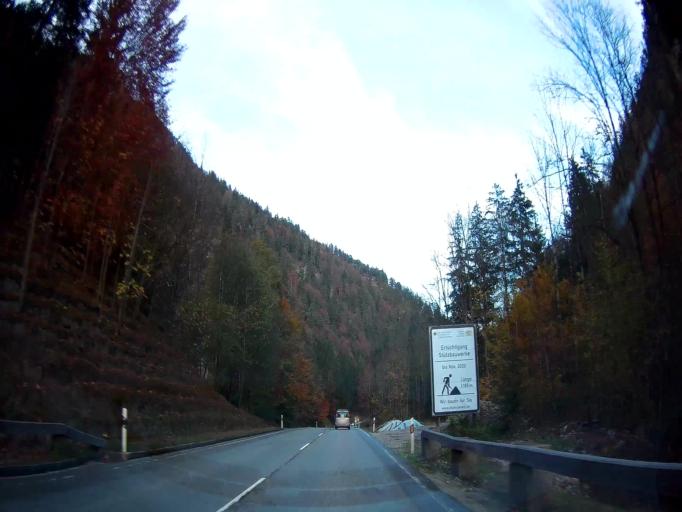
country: DE
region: Bavaria
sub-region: Upper Bavaria
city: Schneizlreuth
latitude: 47.6809
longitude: 12.7760
